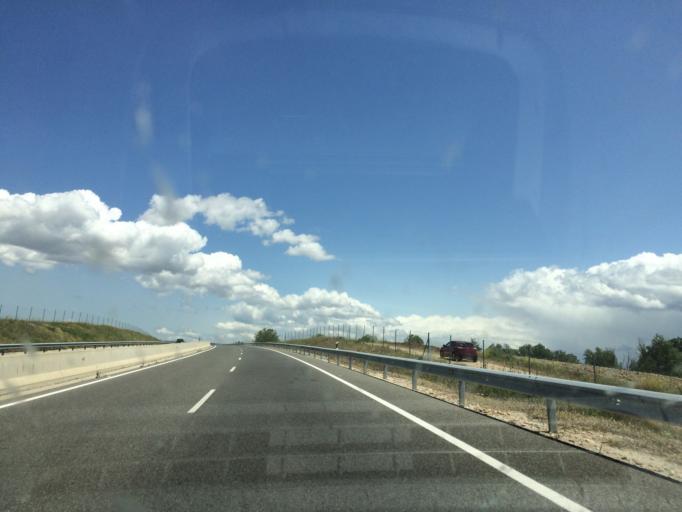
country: ES
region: Madrid
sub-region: Provincia de Madrid
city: Fuente el Saz
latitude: 40.6336
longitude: -3.5315
